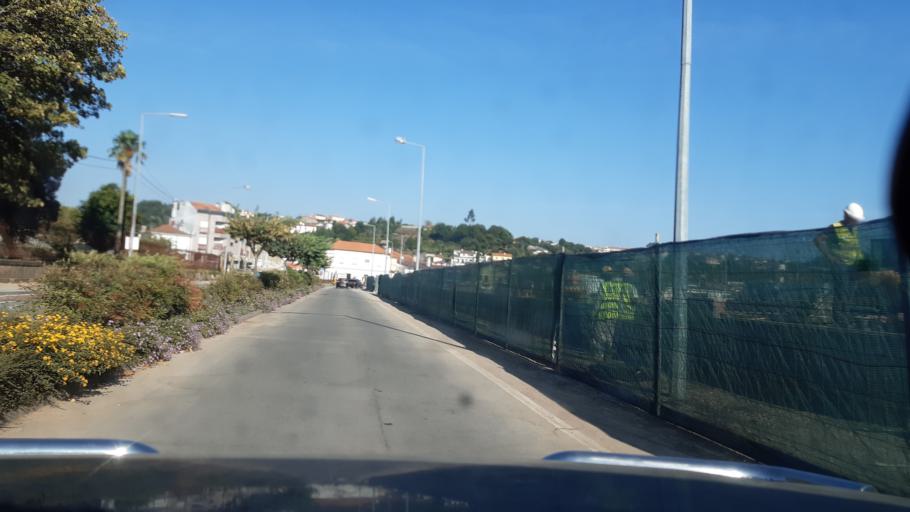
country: PT
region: Aveiro
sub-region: Agueda
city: Agueda
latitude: 40.5729
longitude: -8.4396
